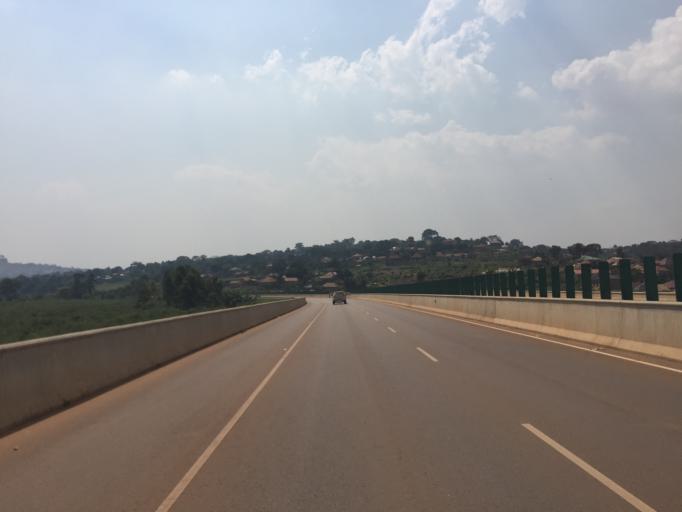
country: UG
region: Central Region
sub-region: Kampala District
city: Kampala
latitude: 0.2368
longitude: 32.6119
